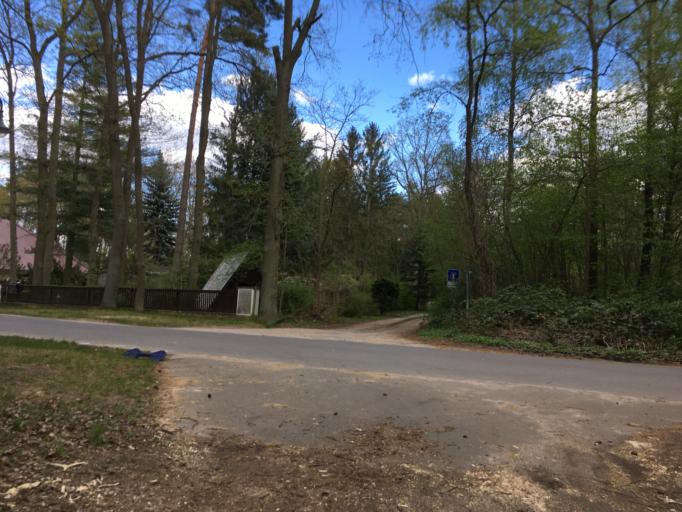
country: DE
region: Brandenburg
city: Wandlitz
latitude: 52.7713
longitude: 13.4372
